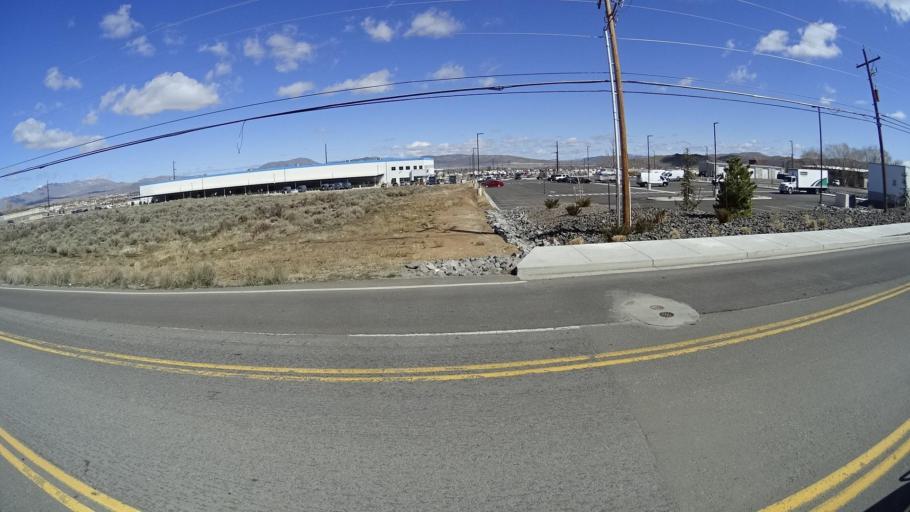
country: US
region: Nevada
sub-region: Washoe County
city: Lemmon Valley
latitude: 39.6135
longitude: -119.8767
